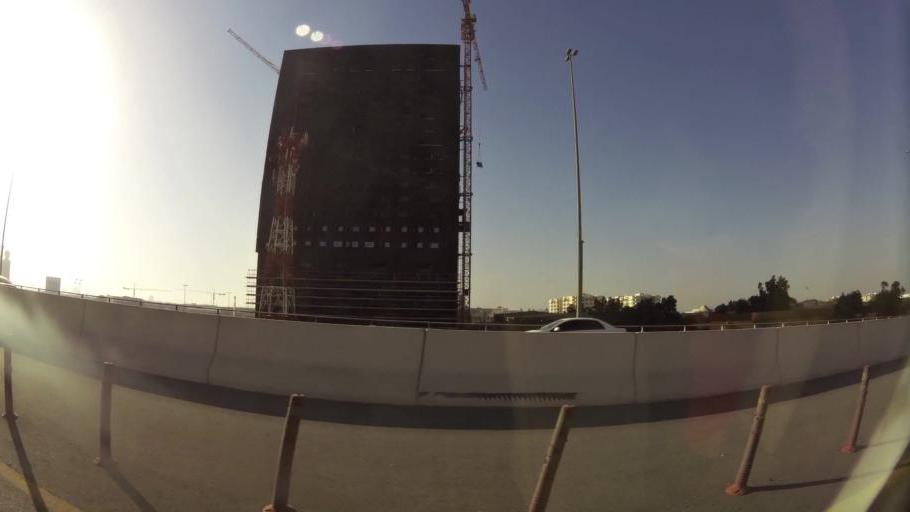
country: AE
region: Ajman
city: Ajman
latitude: 25.3944
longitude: 55.4847
